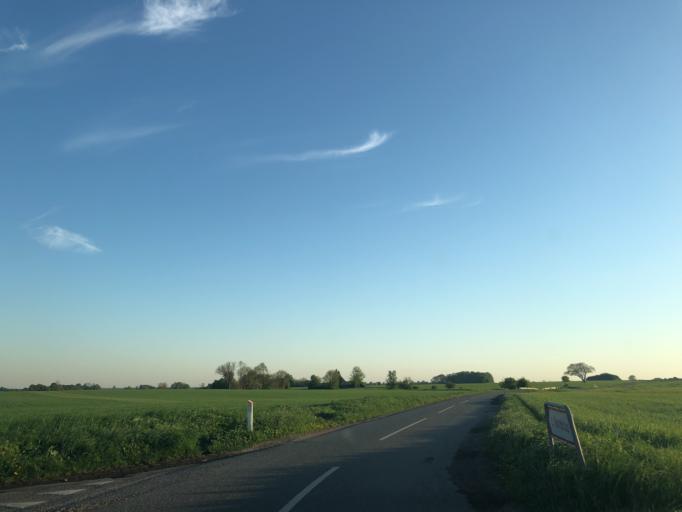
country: DK
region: Zealand
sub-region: Koge Kommune
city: Borup
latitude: 55.4139
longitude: 11.9150
